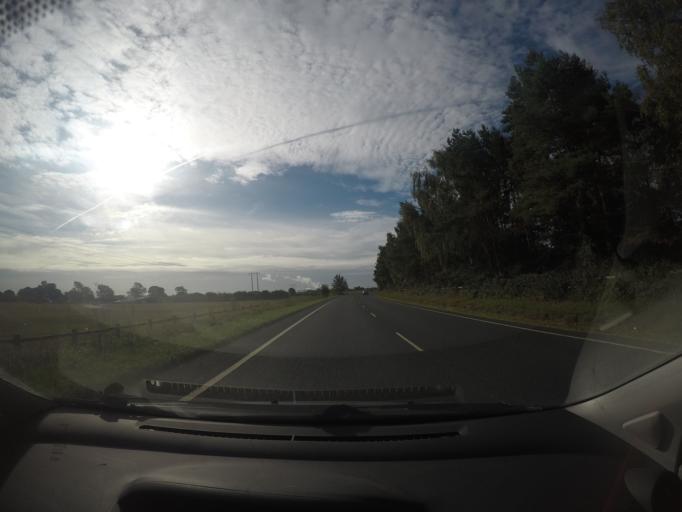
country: GB
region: England
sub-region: North Yorkshire
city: Barlby
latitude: 53.8066
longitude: -1.0368
